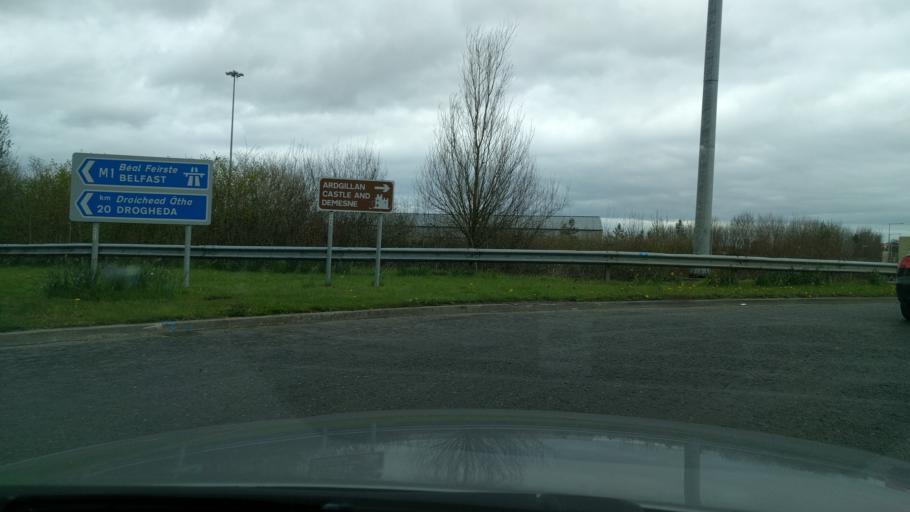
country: IE
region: Leinster
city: Balrothery
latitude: 53.5984
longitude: -6.2216
